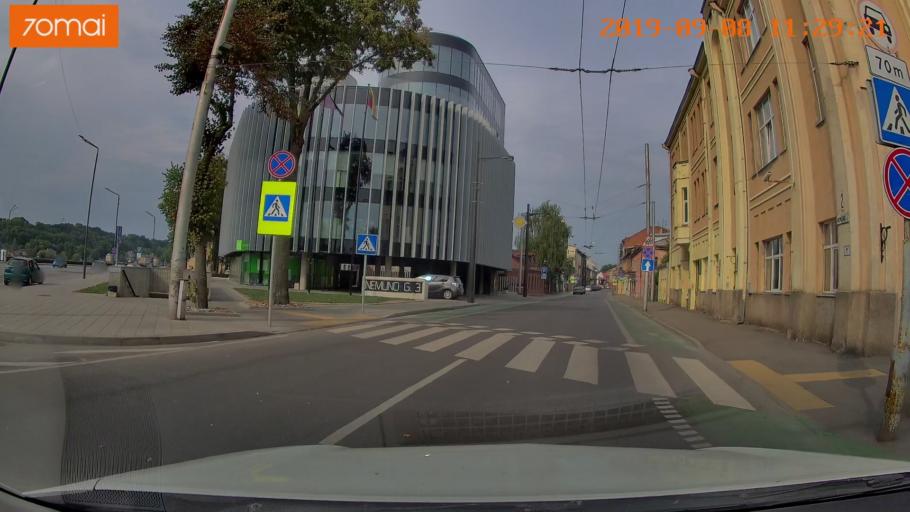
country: LT
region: Kauno apskritis
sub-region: Kaunas
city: Kaunas
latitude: 54.8946
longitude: 23.9023
